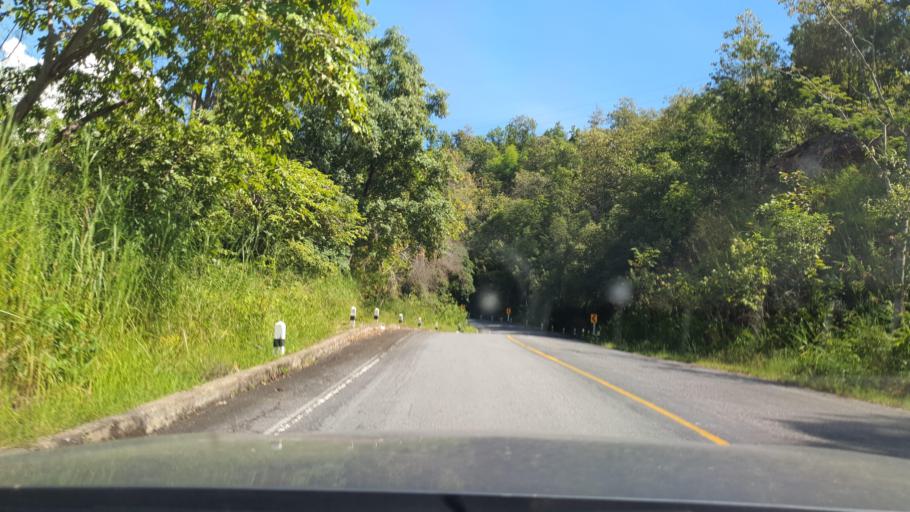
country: TH
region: Chiang Mai
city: Phrao
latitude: 19.3592
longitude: 99.2679
